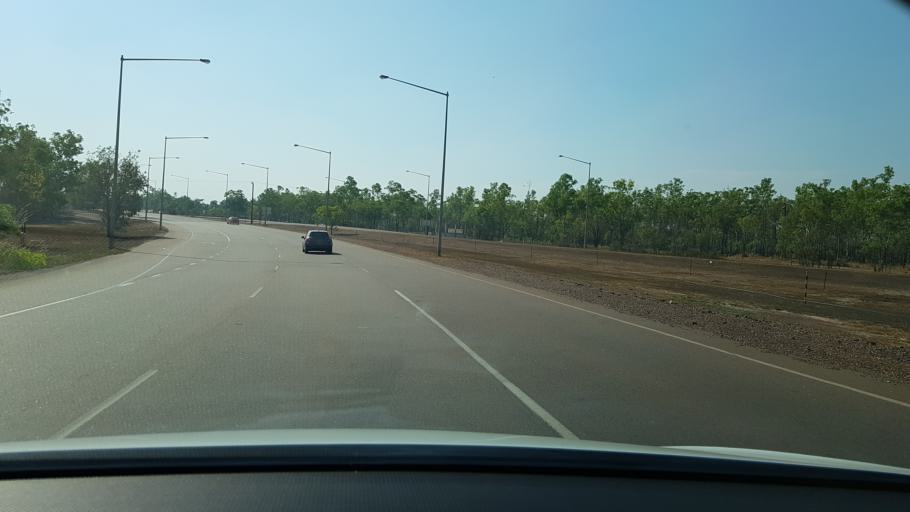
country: AU
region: Northern Territory
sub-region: Palmerston
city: Palmerston
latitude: -12.4633
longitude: 130.9744
